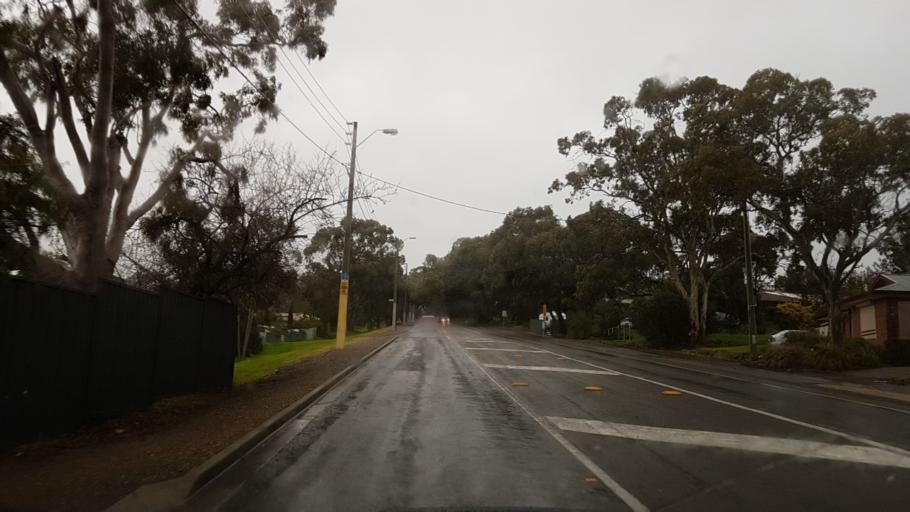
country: AU
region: South Australia
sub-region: Onkaparinga
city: Craigburn Farm
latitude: -35.0873
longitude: 138.5891
